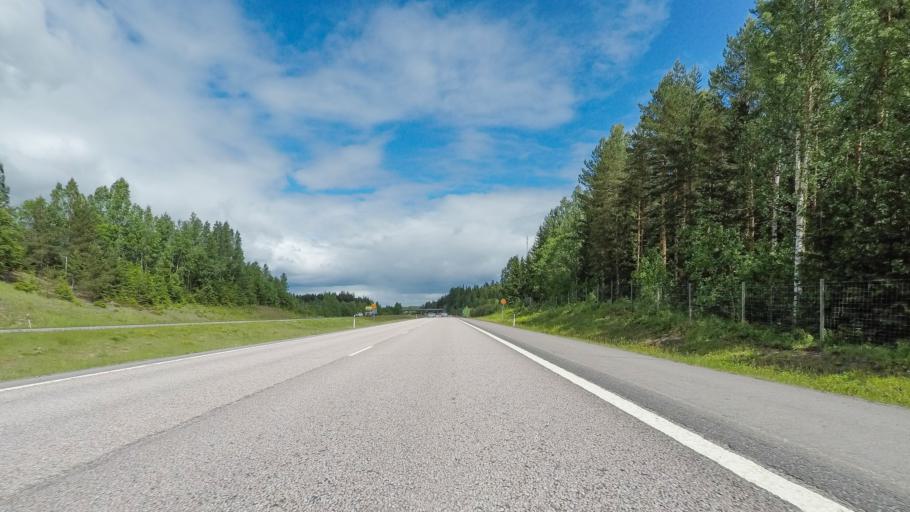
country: FI
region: Uusimaa
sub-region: Helsinki
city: Maentsaelae
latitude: 60.7113
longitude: 25.4228
